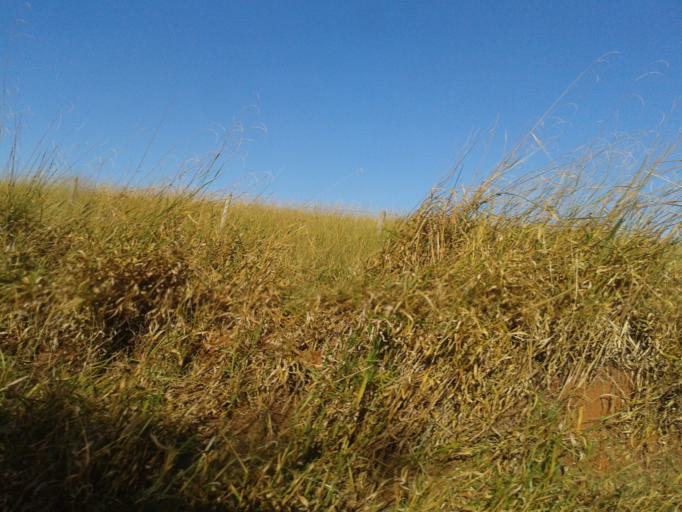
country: BR
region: Minas Gerais
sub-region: Centralina
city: Centralina
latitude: -18.7526
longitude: -49.1042
